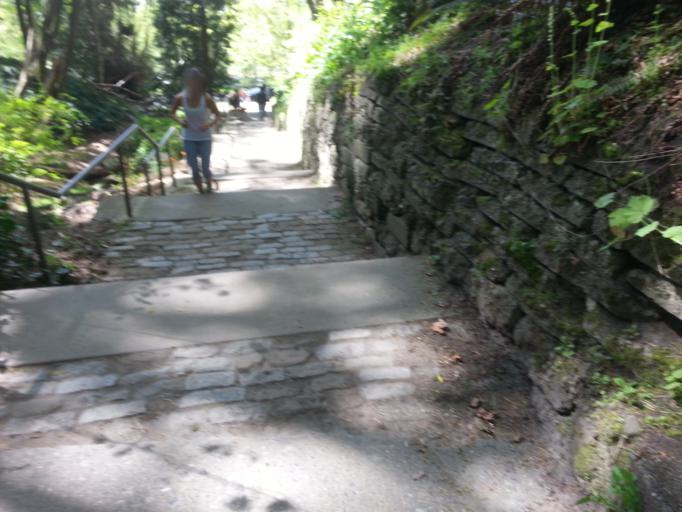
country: US
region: Washington
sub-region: King County
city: Shoreline
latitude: 47.6903
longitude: -122.4006
